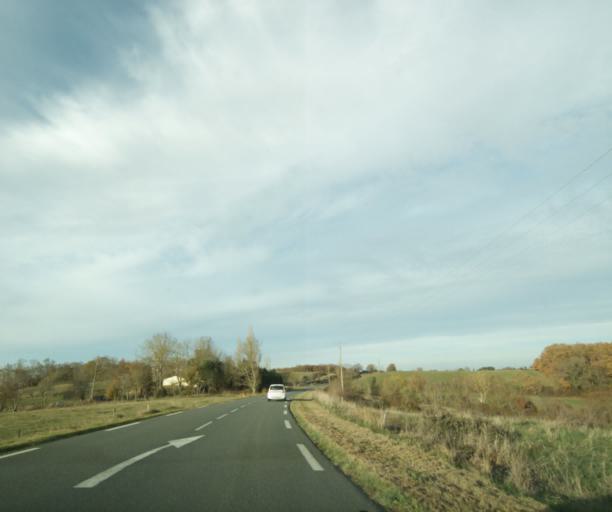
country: FR
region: Midi-Pyrenees
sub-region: Departement du Gers
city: Eauze
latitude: 43.7970
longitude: 0.0987
